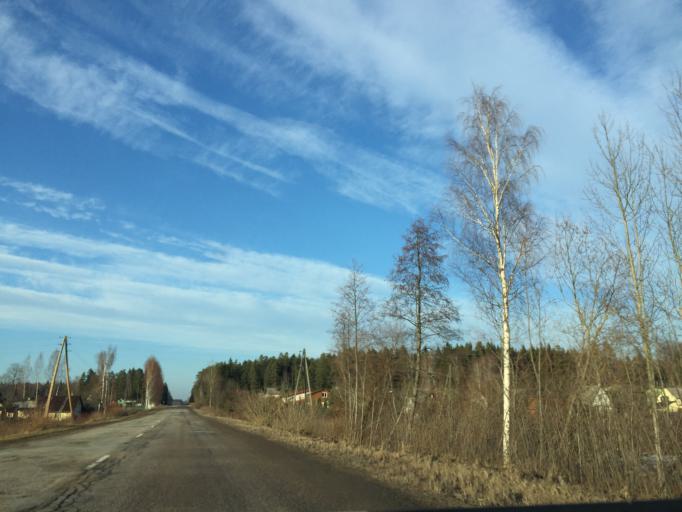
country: LV
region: Lecava
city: Iecava
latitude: 56.7150
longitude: 24.1121
